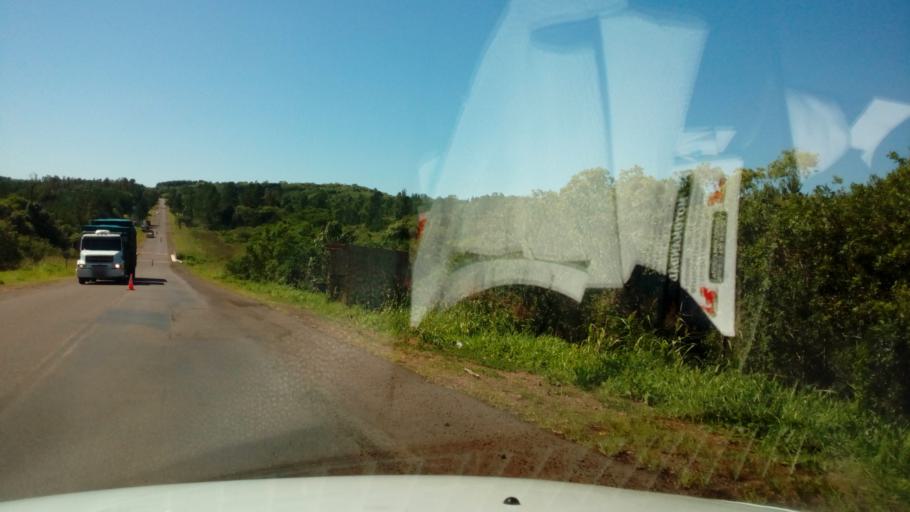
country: AR
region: Misiones
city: Almafuerte
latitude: -27.5497
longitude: -55.4269
